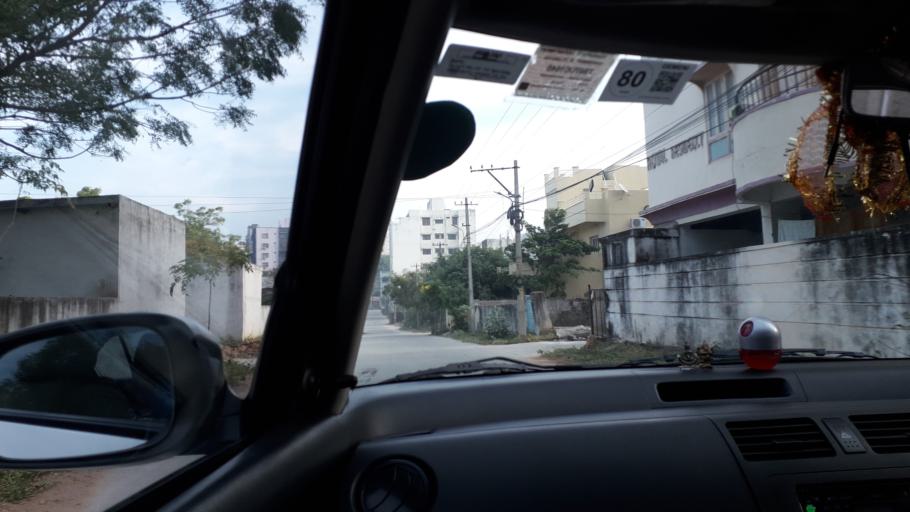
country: IN
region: Telangana
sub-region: Hyderabad
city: Hyderabad
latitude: 17.3923
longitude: 78.3851
